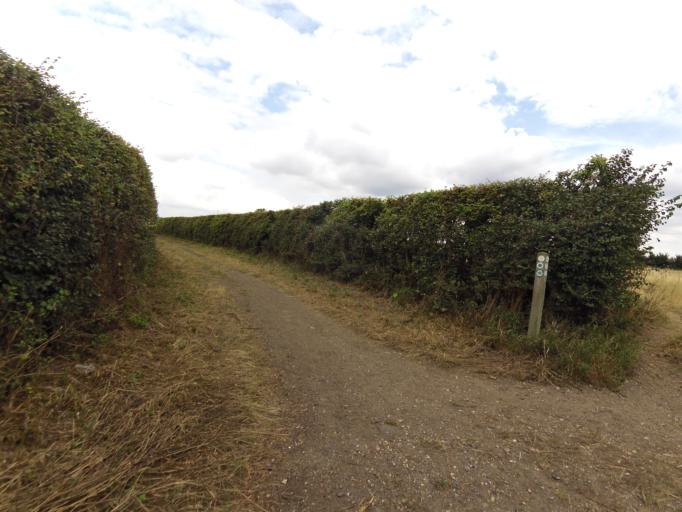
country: GB
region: England
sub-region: Hertfordshire
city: Shenley AV
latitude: 51.7061
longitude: -0.2814
